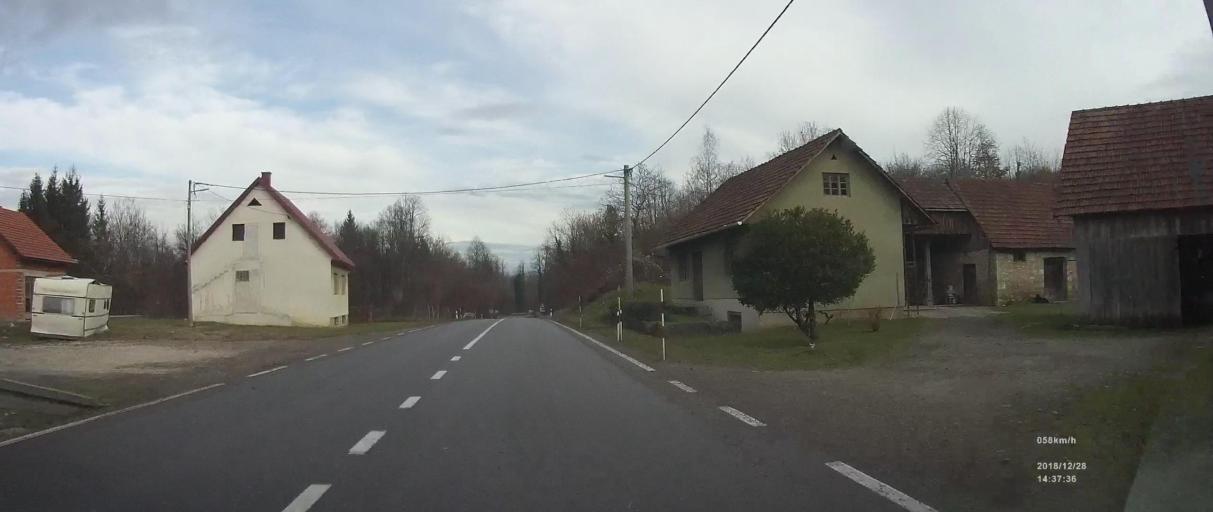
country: HR
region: Primorsko-Goranska
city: Vrbovsko
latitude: 45.4214
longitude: 15.2118
